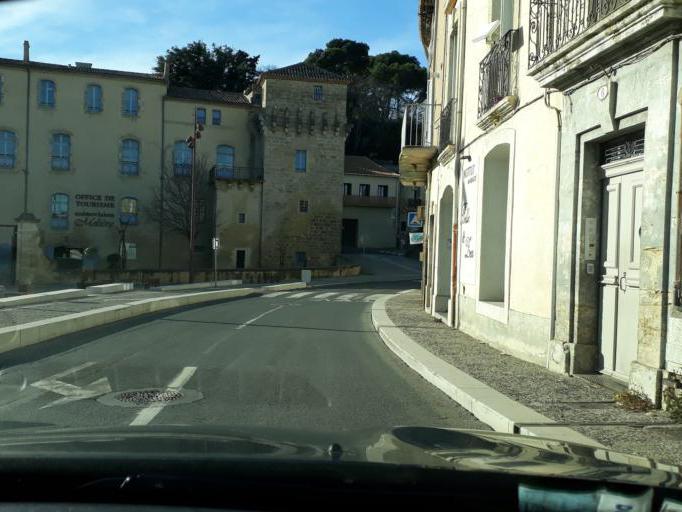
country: FR
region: Languedoc-Roussillon
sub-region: Departement de l'Herault
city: Pezenas
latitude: 43.4621
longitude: 3.4241
